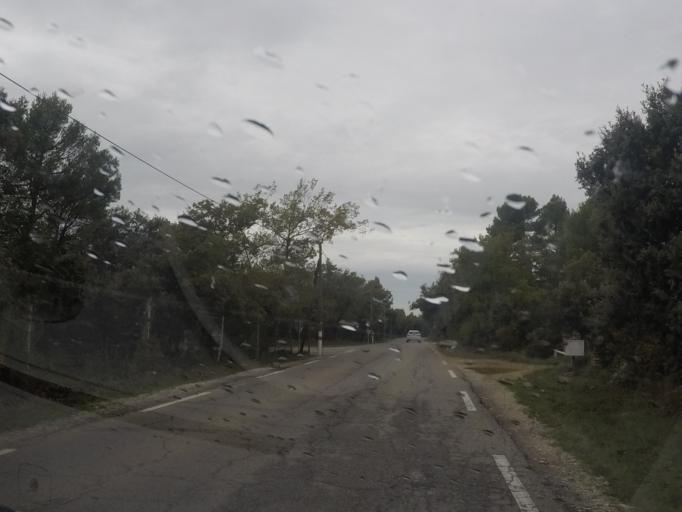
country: FR
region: Provence-Alpes-Cote d'Azur
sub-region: Departement du Vaucluse
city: Bonnieux
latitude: 43.8168
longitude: 5.3220
